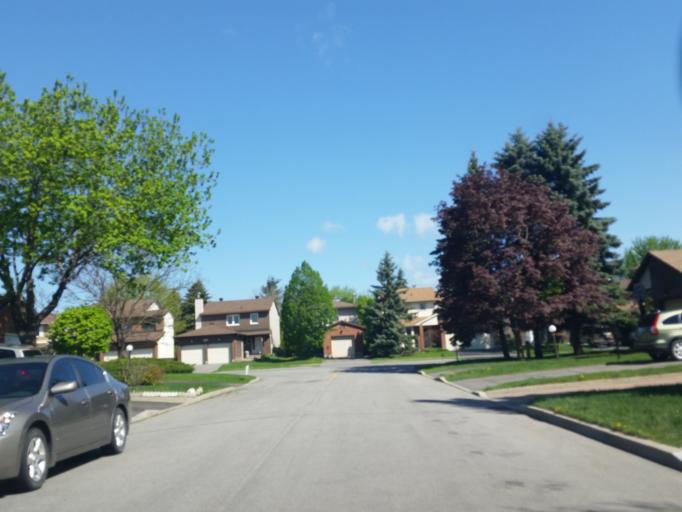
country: CA
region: Ontario
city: Ottawa
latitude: 45.3492
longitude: -75.7140
